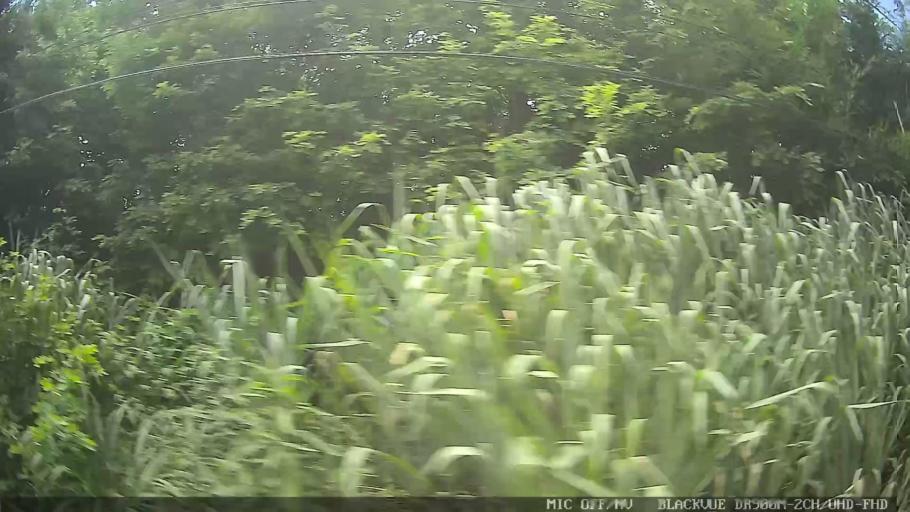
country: BR
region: Sao Paulo
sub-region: Santa Isabel
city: Santa Isabel
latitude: -23.4171
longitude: -46.2123
